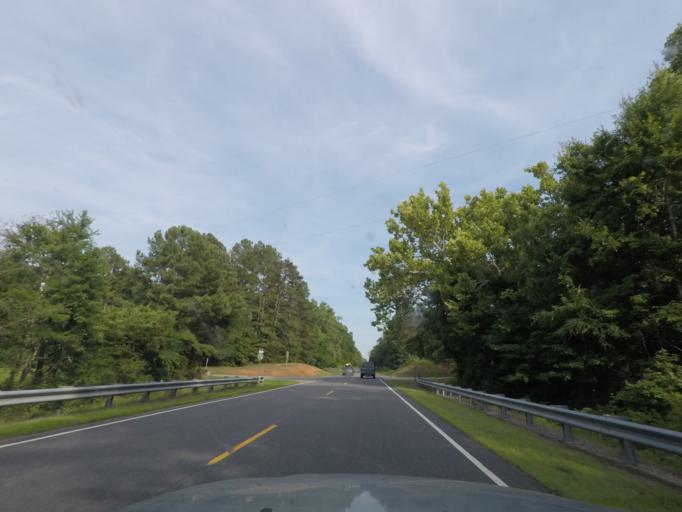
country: US
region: Virginia
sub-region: Mecklenburg County
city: Clarksville
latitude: 36.6945
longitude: -78.6239
